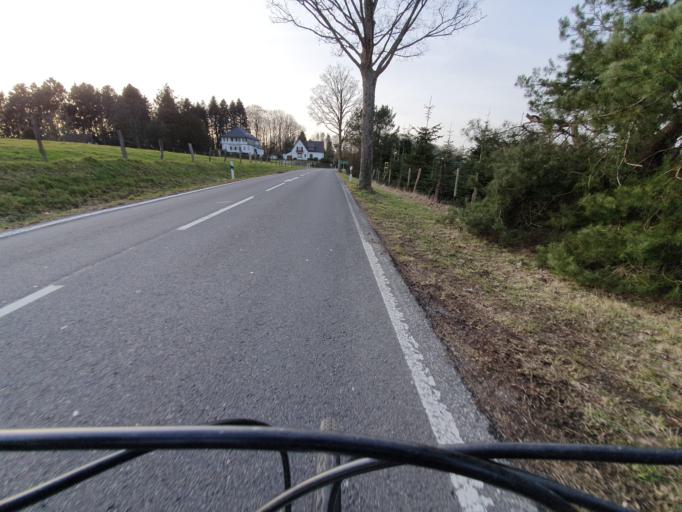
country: DE
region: North Rhine-Westphalia
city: Burscheid
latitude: 51.0889
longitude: 7.1617
